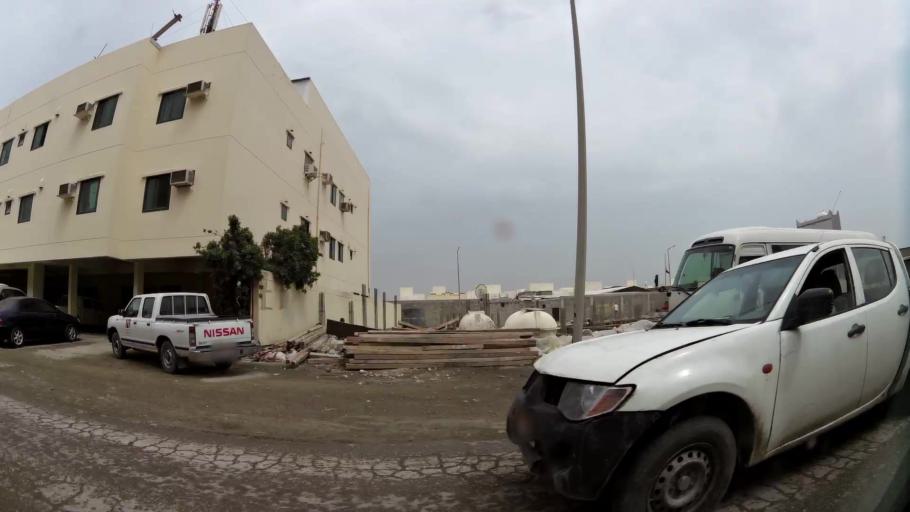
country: BH
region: Northern
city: Ar Rifa'
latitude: 26.1390
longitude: 50.5882
